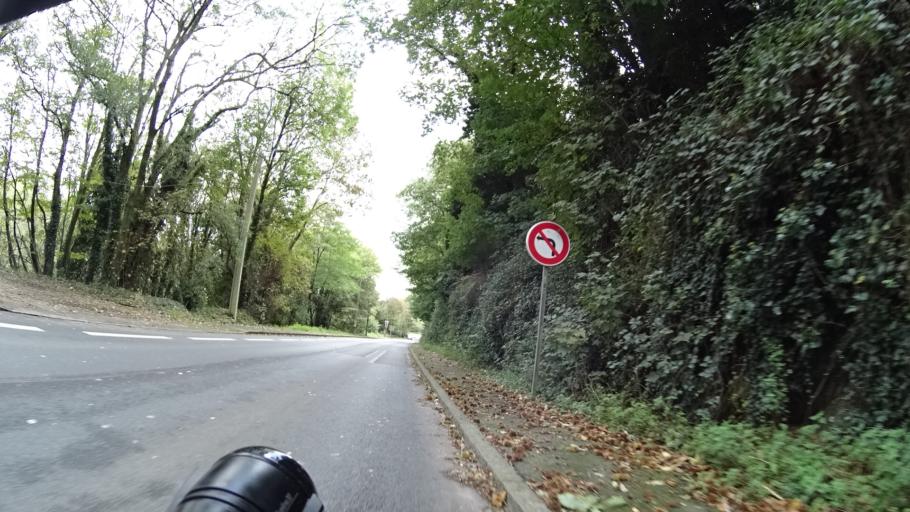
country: FR
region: Brittany
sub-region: Departement du Finistere
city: Brest
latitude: 48.3984
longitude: -4.4395
